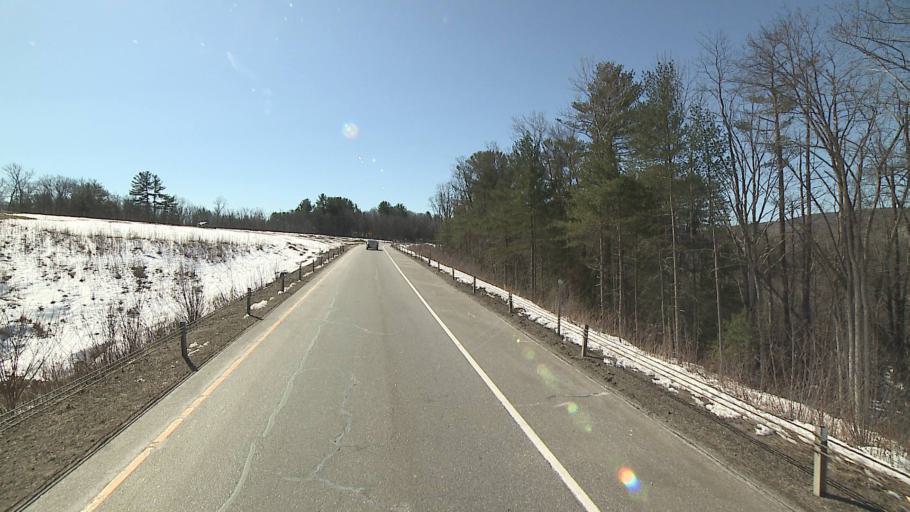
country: US
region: Connecticut
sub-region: Litchfield County
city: Winsted
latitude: 41.8778
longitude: -73.0728
